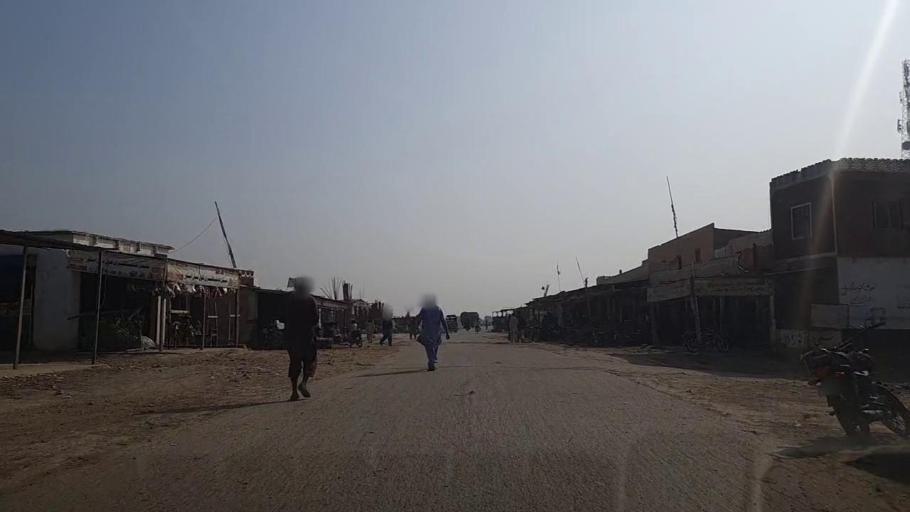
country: PK
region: Sindh
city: Keti Bandar
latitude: 24.2377
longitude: 67.6076
